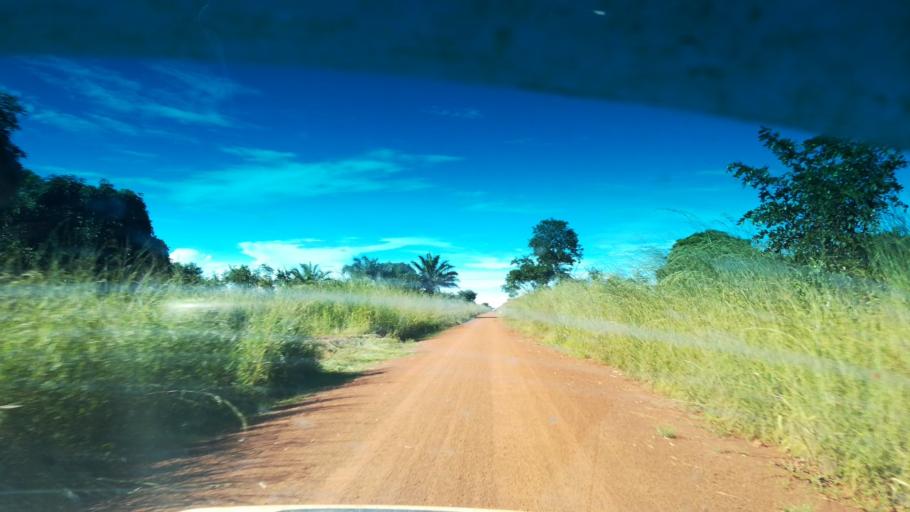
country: ZM
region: Luapula
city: Nchelenge
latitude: -9.3341
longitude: 28.2376
